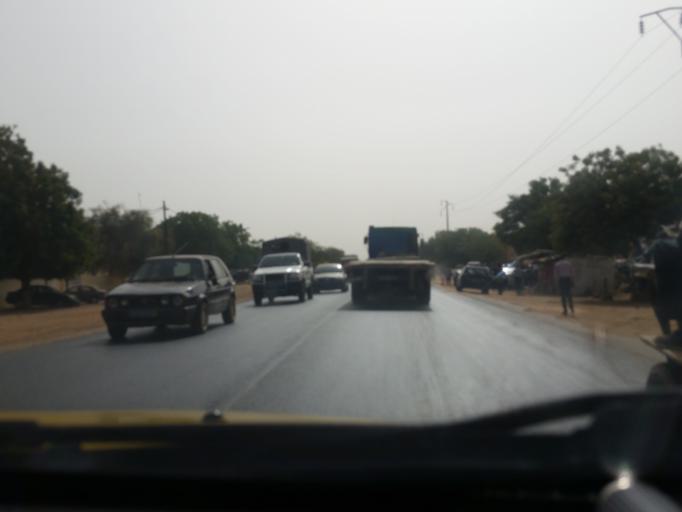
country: SN
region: Thies
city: Pout
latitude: 14.7366
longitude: -17.1474
